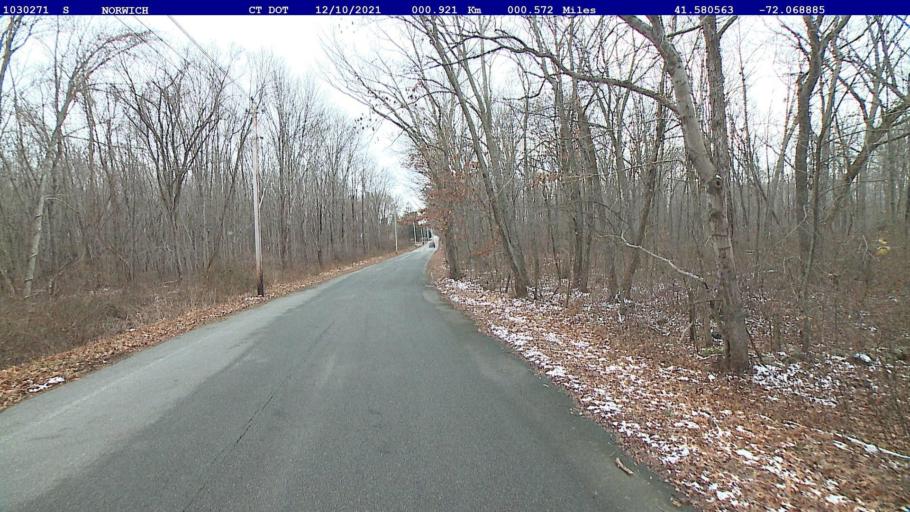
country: US
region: Connecticut
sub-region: New London County
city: Baltic
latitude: 41.5806
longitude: -72.0689
